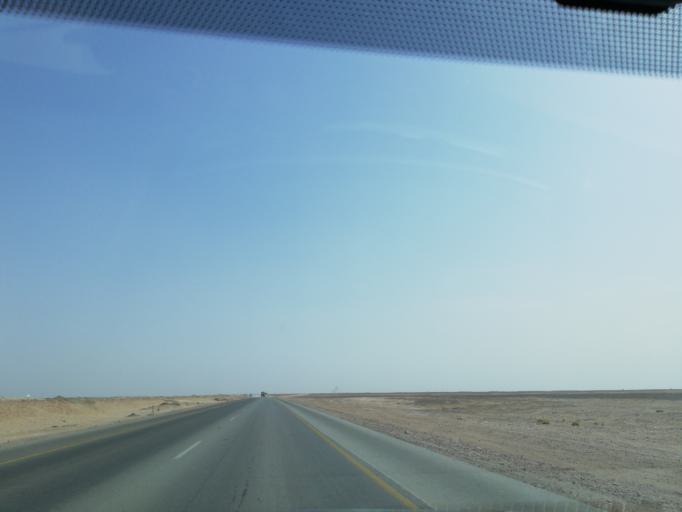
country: OM
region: Muhafazat ad Dakhiliyah
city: Adam
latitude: 21.7233
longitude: 57.3288
